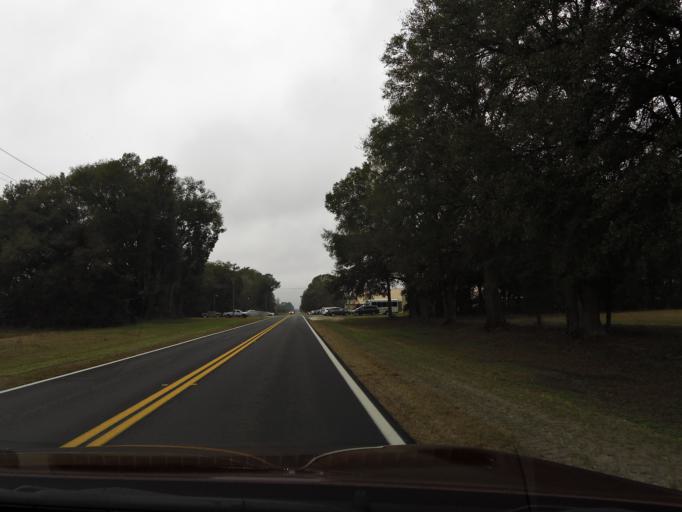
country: US
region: Florida
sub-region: Gilchrist County
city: Trenton
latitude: 29.7960
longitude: -82.8772
